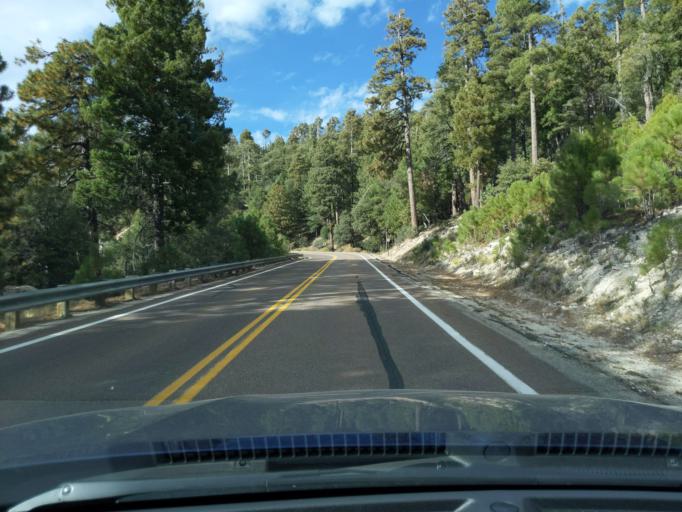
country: US
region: Arizona
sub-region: Pima County
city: Tanque Verde
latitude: 32.4083
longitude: -110.7042
